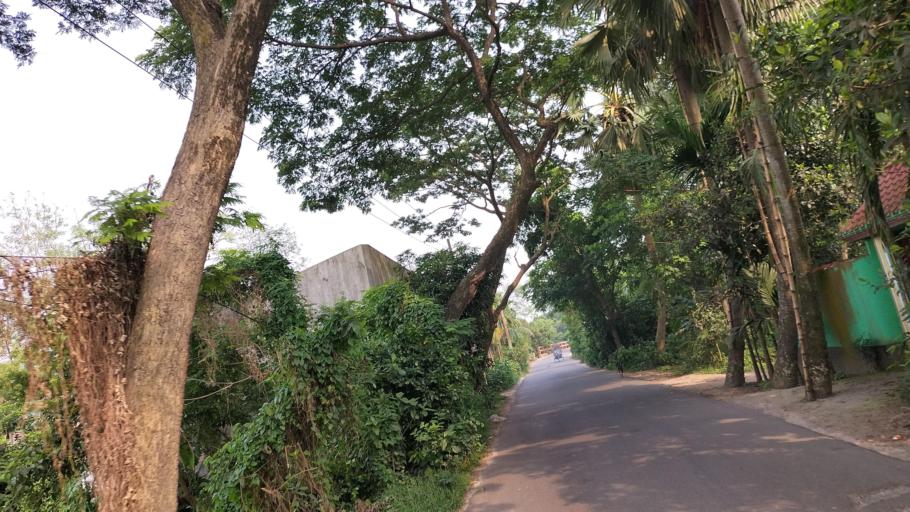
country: BD
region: Dhaka
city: Azimpur
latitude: 23.6767
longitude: 90.3171
